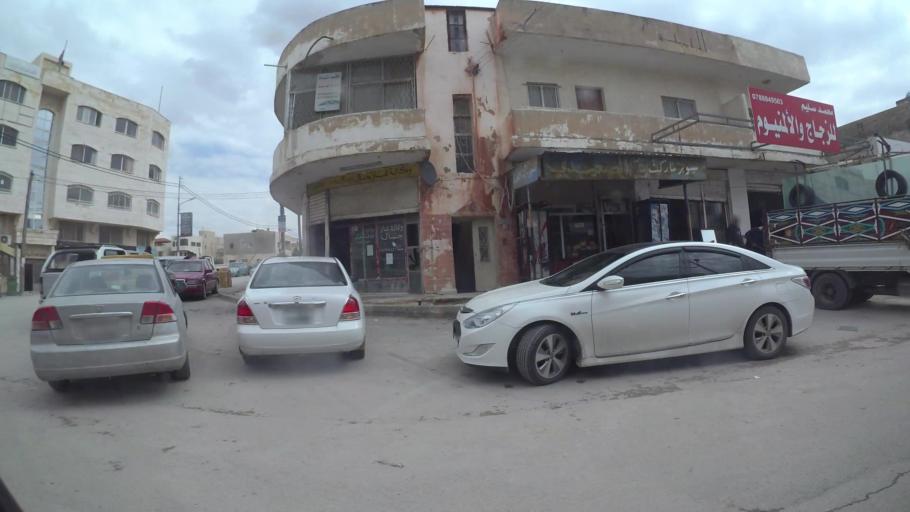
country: JO
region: Amman
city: Al Jubayhah
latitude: 32.0562
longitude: 35.8348
